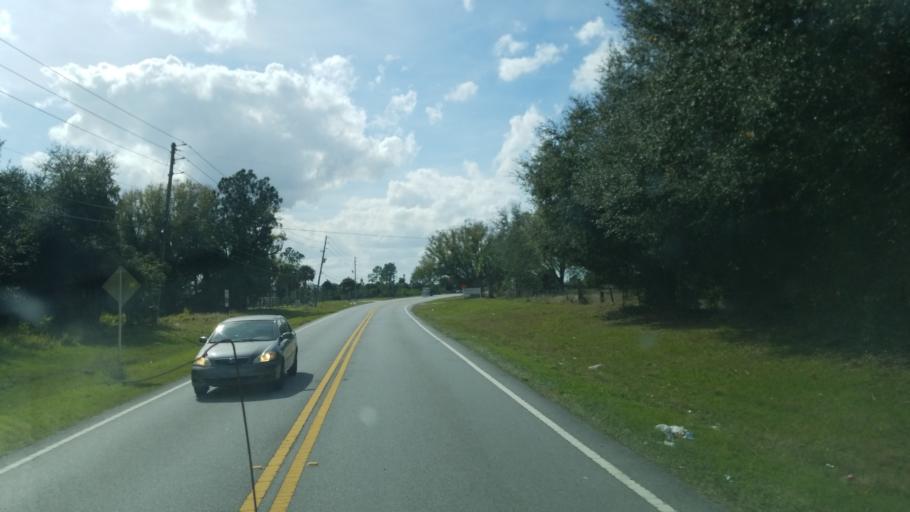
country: US
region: Florida
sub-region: Polk County
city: Lake Wales
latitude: 27.9584
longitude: -81.6096
